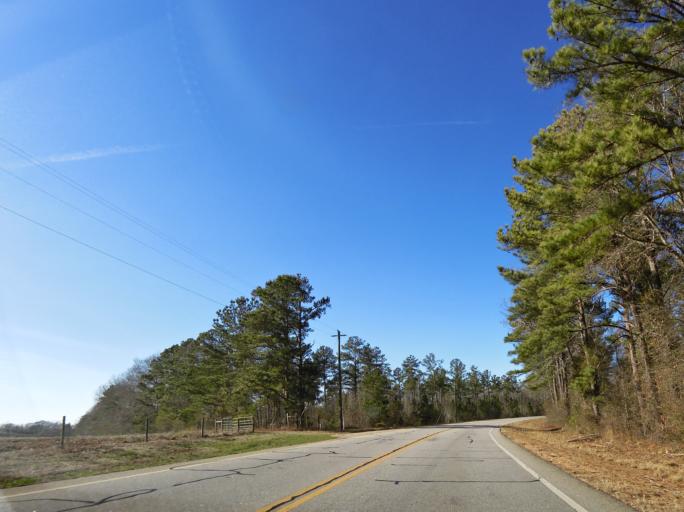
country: US
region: Georgia
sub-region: Lamar County
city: Barnesville
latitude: 32.9073
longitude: -84.1206
